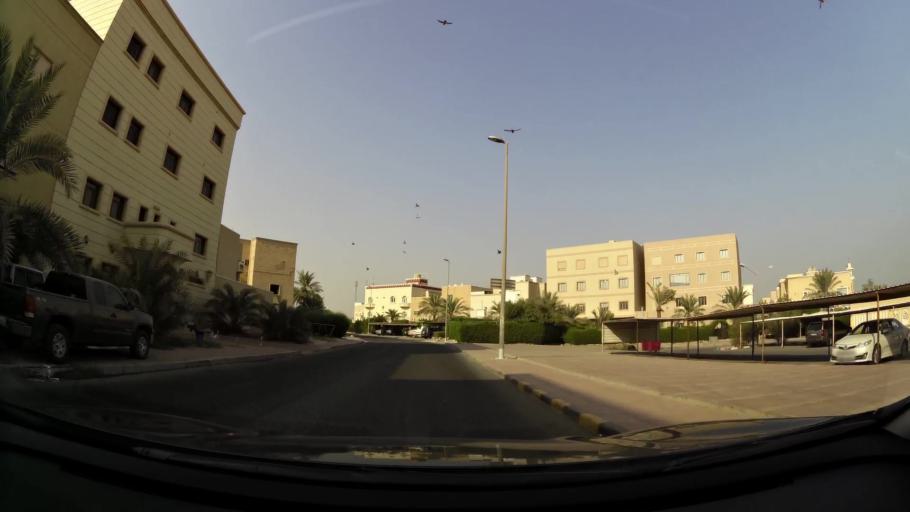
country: KW
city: Al Funaytis
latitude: 29.2174
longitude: 48.0833
